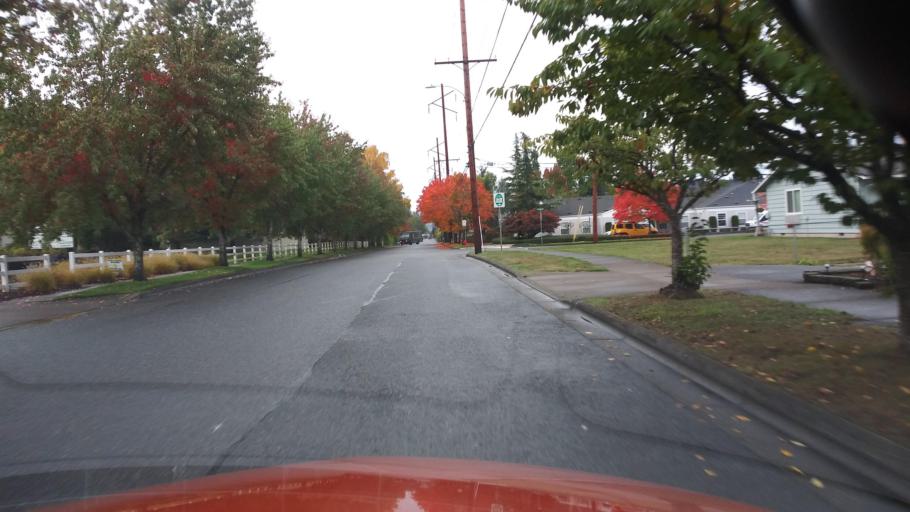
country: US
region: Oregon
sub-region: Washington County
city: Forest Grove
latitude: 45.5230
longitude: -123.0881
